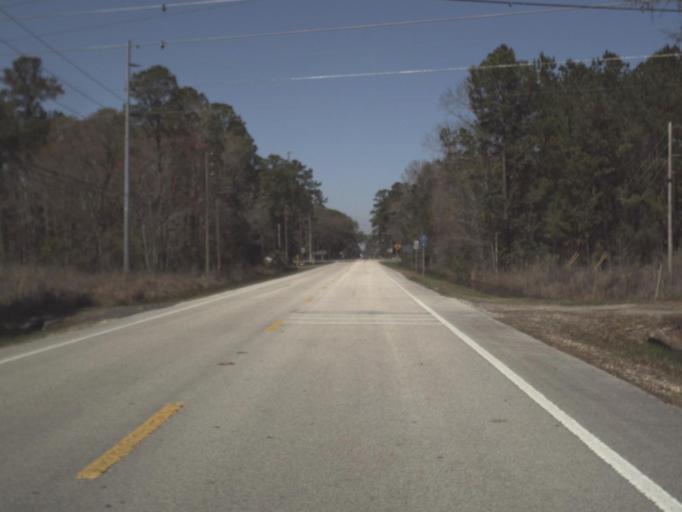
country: US
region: Florida
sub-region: Leon County
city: Woodville
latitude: 30.1879
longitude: -84.2147
